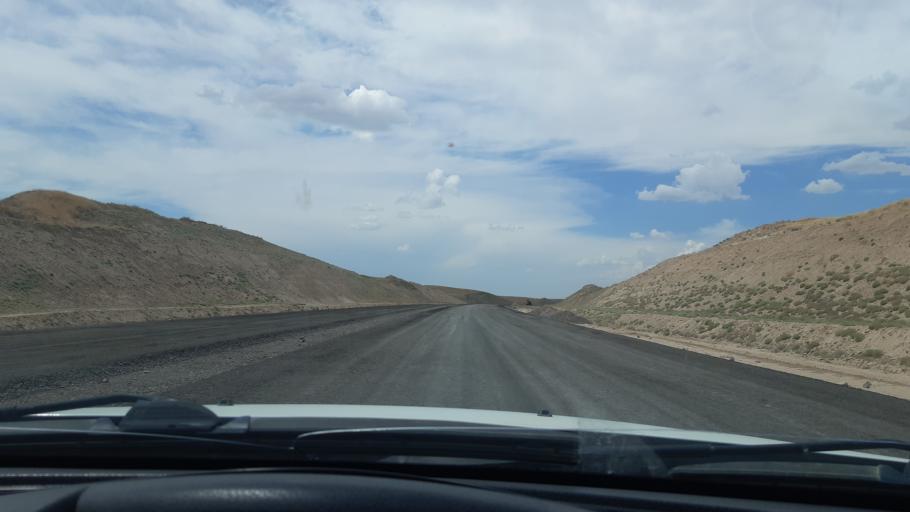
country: KG
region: Chuy
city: Bystrovka
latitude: 43.3206
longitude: 75.8878
